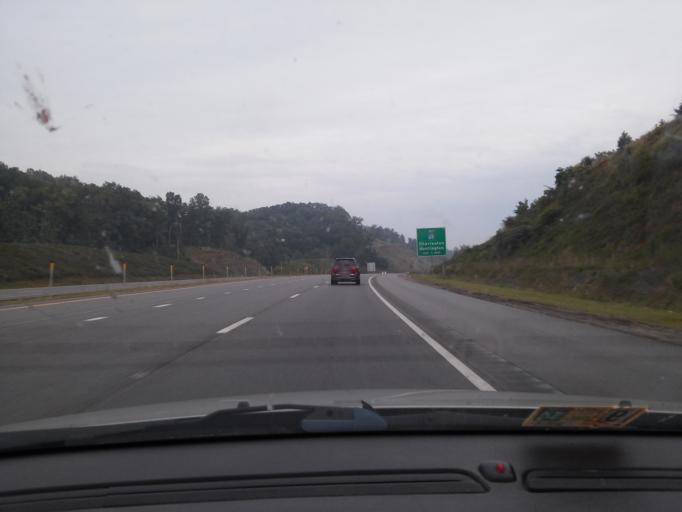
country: US
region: West Virginia
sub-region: Putnam County
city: Teays Valley
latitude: 38.4720
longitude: -81.9130
